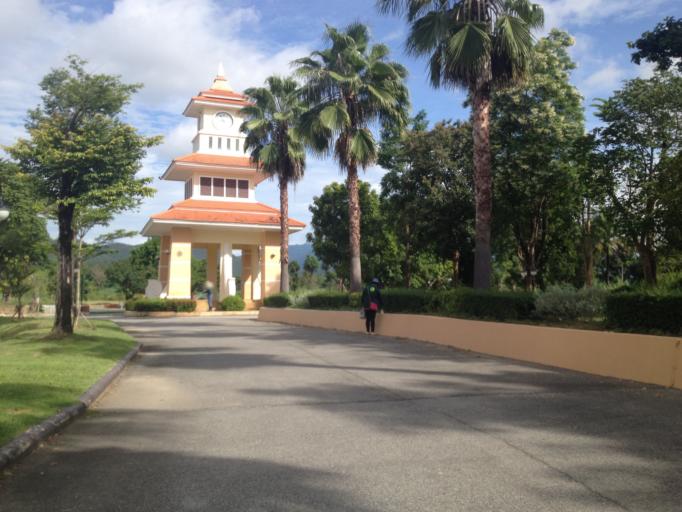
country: TH
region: Chiang Mai
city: Hang Dong
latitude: 18.7097
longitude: 98.9089
